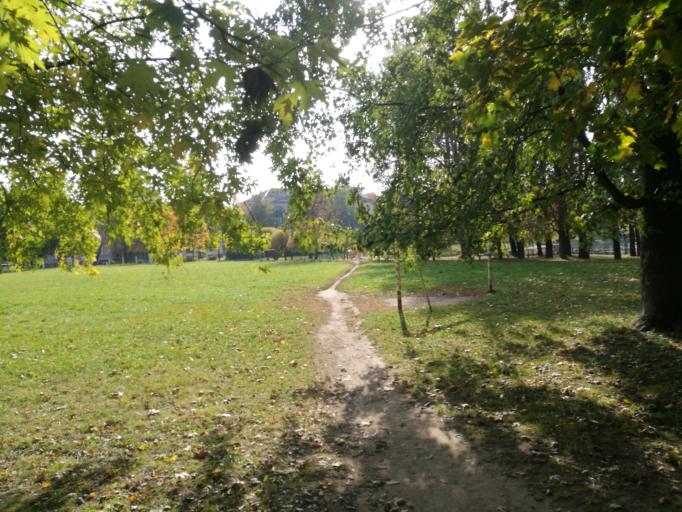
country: BY
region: Minsk
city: Minsk
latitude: 53.8972
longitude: 27.5177
